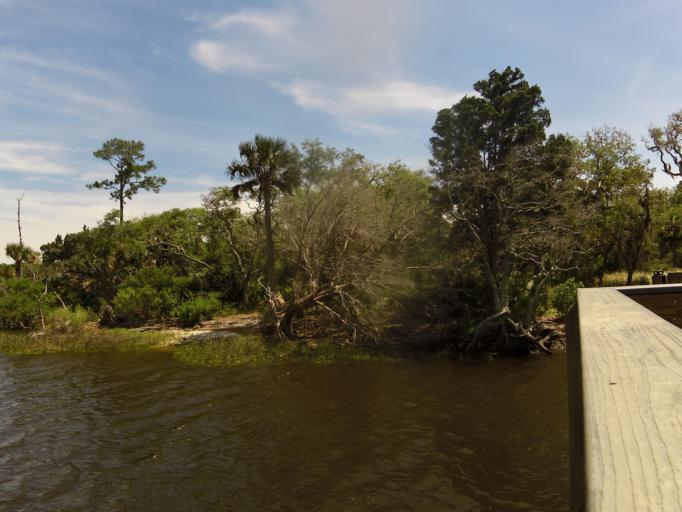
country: US
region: Florida
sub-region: Nassau County
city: Yulee
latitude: 30.5008
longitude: -81.4971
